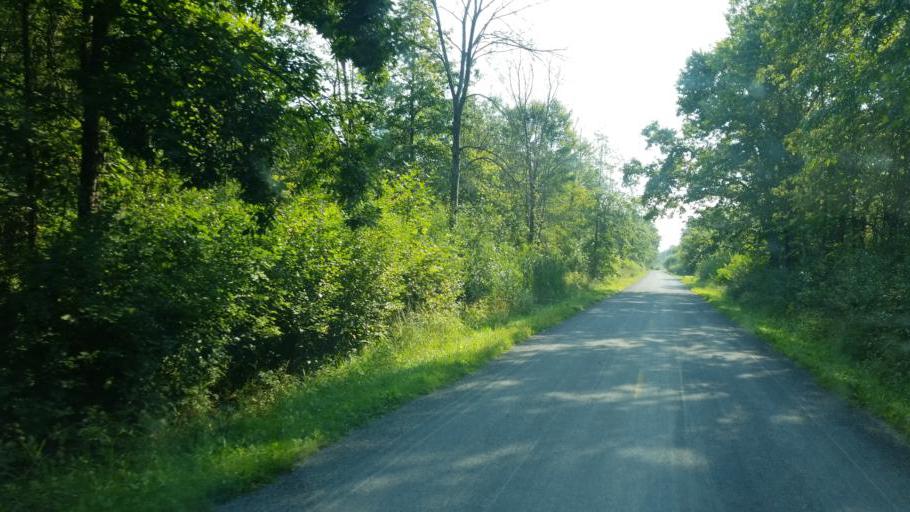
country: US
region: Ohio
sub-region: Ashtabula County
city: Orwell
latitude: 41.4755
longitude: -80.9096
